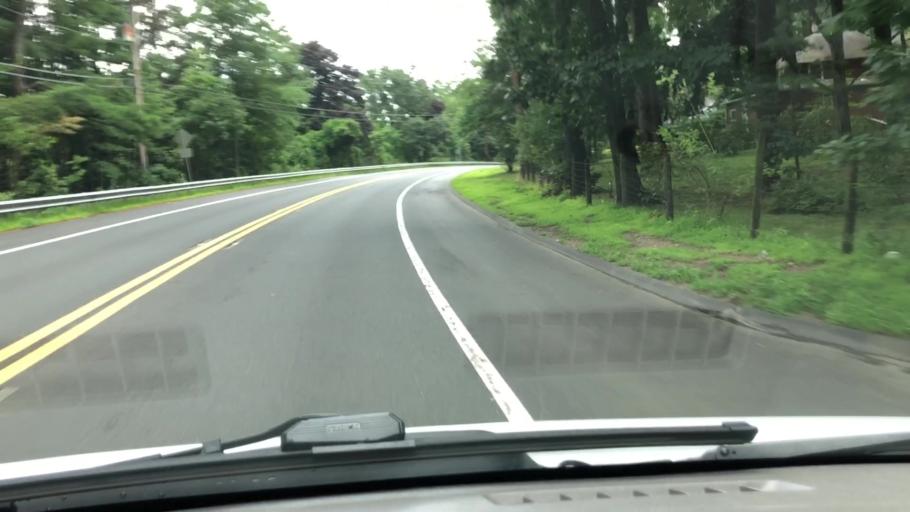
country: US
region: Massachusetts
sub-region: Hampshire County
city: Northampton
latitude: 42.3593
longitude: -72.6383
